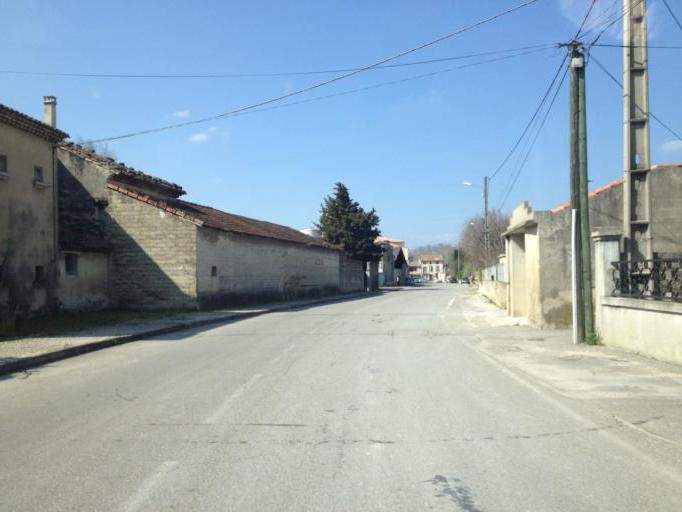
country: FR
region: Provence-Alpes-Cote d'Azur
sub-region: Departement du Vaucluse
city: Jonquieres
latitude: 44.1160
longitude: 4.9034
